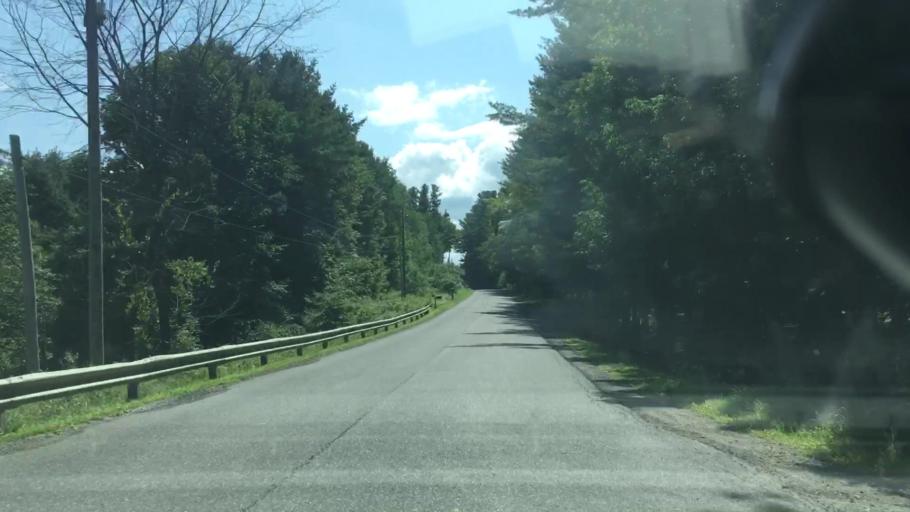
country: US
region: Maine
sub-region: Somerset County
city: Skowhegan
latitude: 44.6907
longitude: -69.6925
